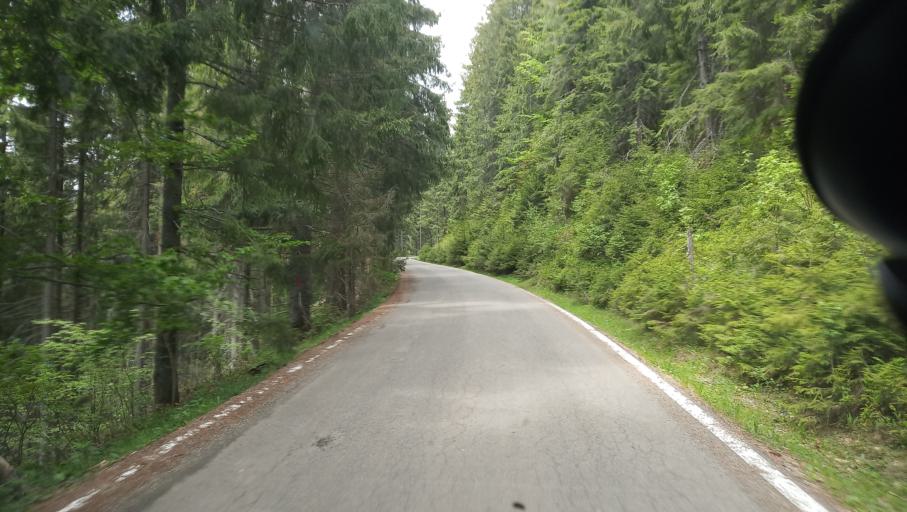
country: RO
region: Alba
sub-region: Comuna Horea
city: Horea
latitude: 46.5208
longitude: 22.8888
